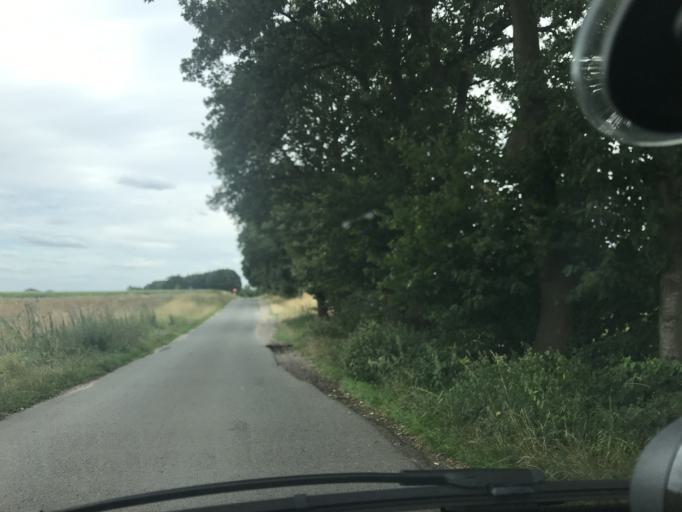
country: DE
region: Lower Saxony
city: Moisburg
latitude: 53.4033
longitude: 9.7094
